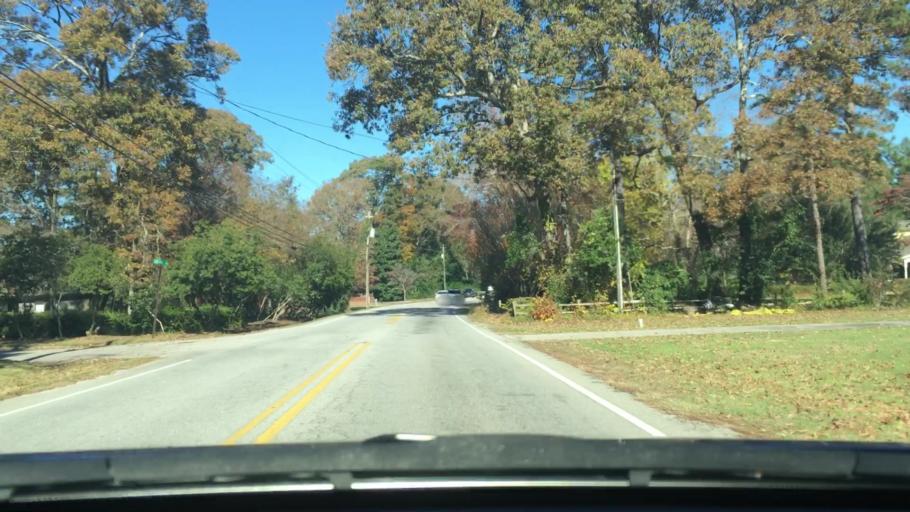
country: US
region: South Carolina
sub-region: Sumter County
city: South Sumter
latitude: 33.8977
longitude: -80.3698
